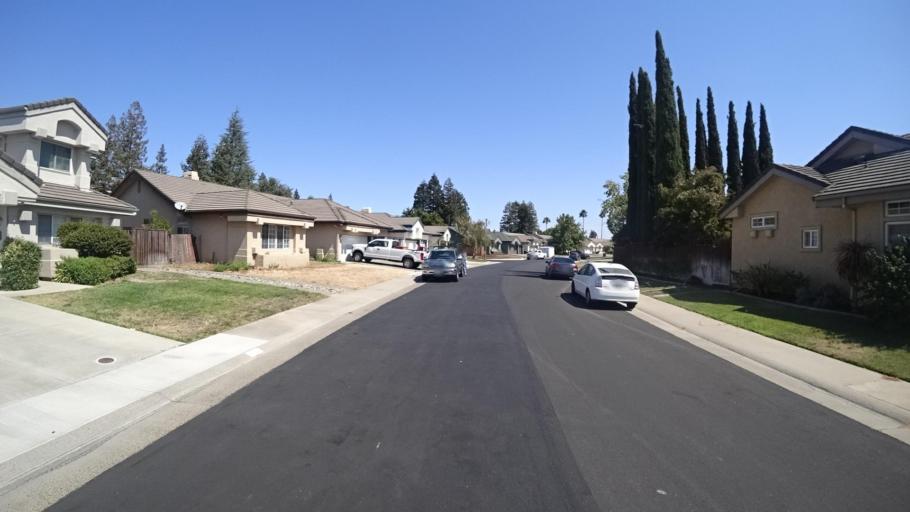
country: US
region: California
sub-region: Sacramento County
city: Laguna
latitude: 38.4114
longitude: -121.4145
